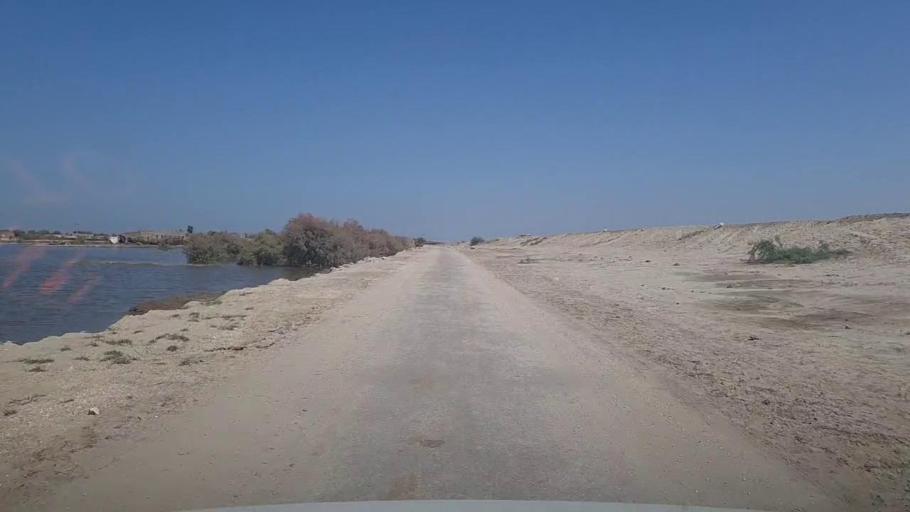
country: PK
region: Sindh
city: Kashmor
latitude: 28.2823
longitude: 69.4553
